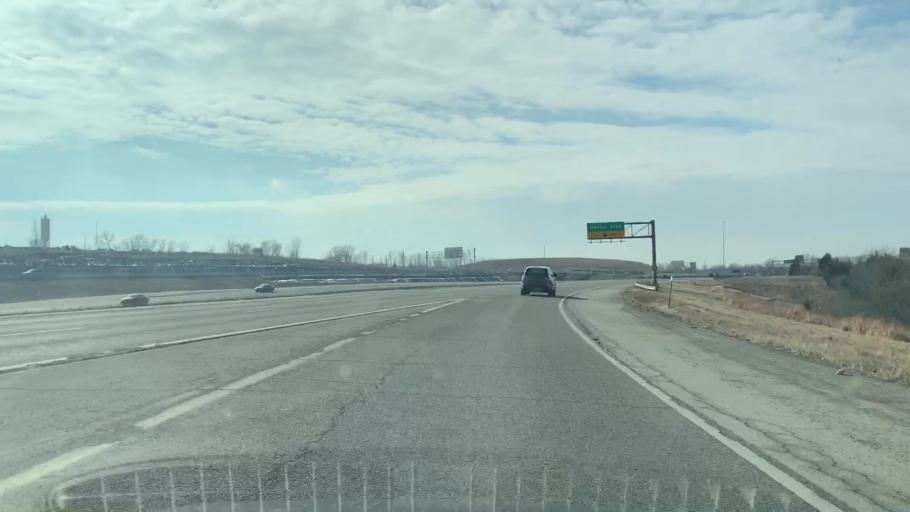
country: US
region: Kansas
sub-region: Johnson County
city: Lenexa
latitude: 38.9437
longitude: -94.7765
